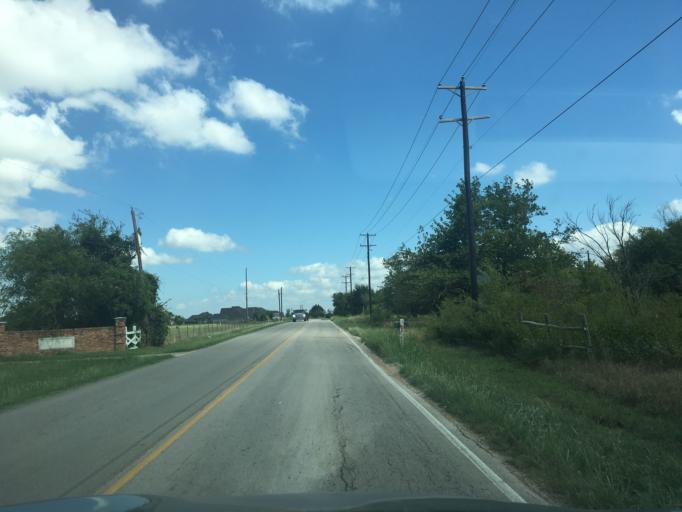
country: US
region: Texas
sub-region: Dallas County
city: Sachse
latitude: 32.9615
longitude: -96.5591
